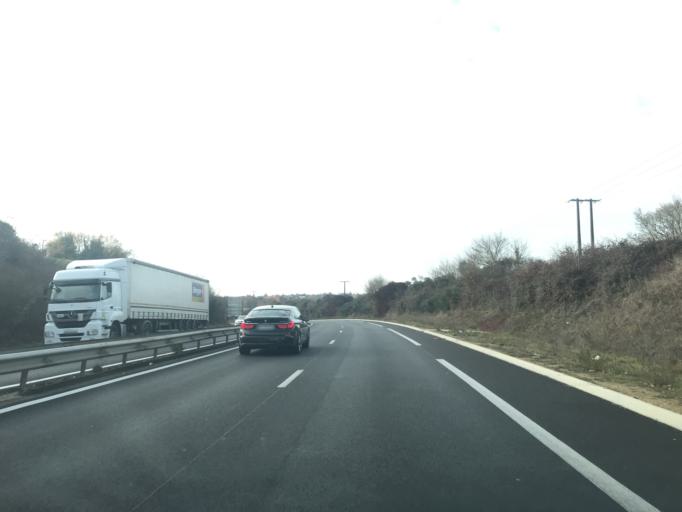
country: FR
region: Poitou-Charentes
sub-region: Departement des Deux-Sevres
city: Niort
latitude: 46.3376
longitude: -0.4594
